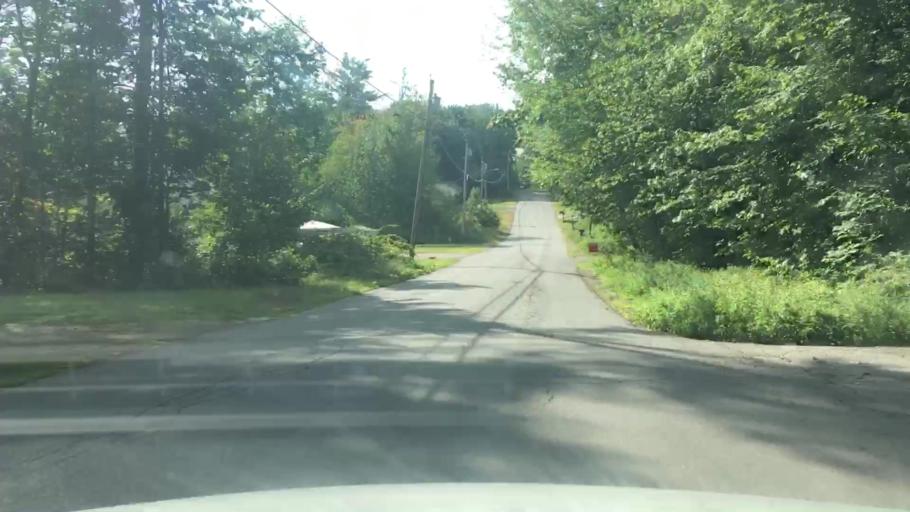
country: US
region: Maine
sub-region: Kennebec County
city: Gardiner
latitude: 44.1677
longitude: -69.8132
